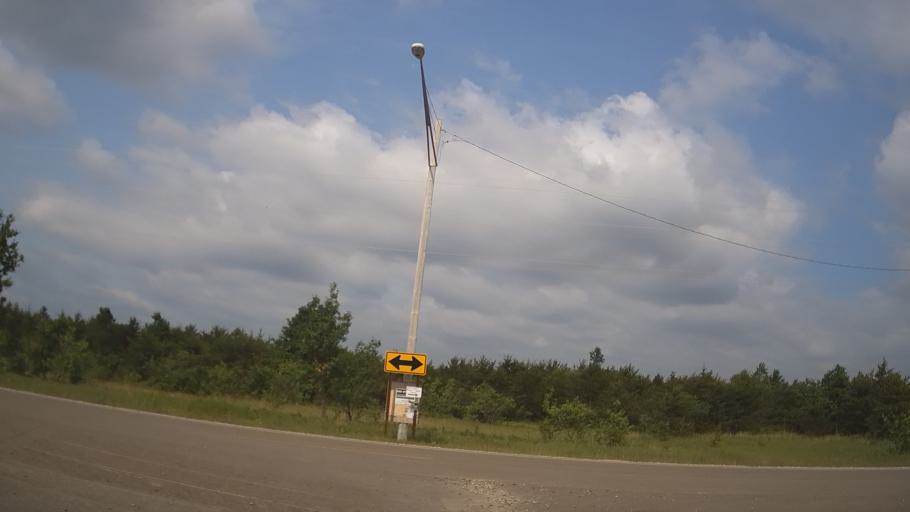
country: US
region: Michigan
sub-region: Roscommon County
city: Saint Helen
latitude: 44.4070
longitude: -84.4101
